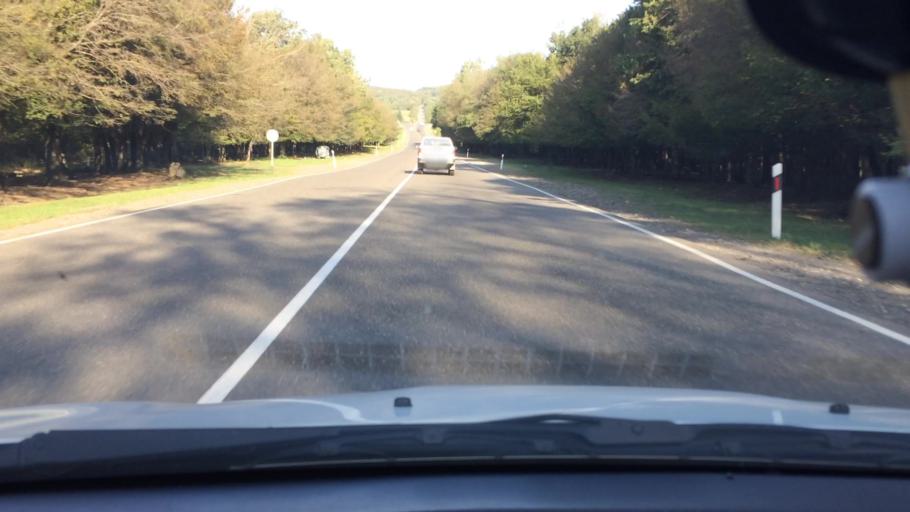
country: GE
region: Imereti
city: Kutaisi
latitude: 42.2350
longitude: 42.7722
